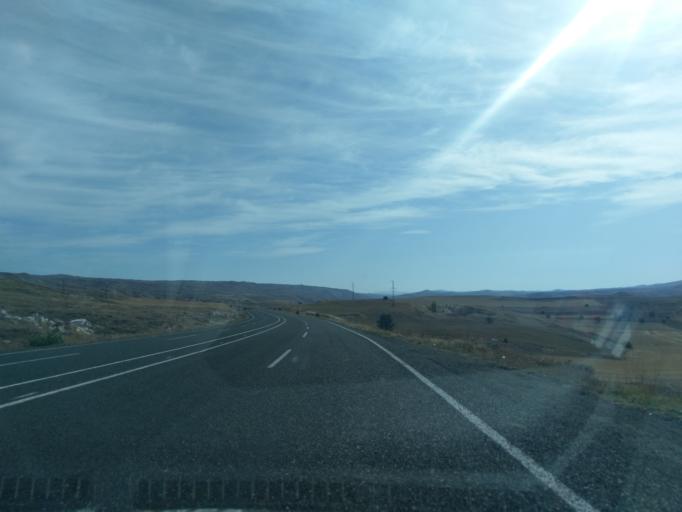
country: TR
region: Sivas
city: Zara
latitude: 39.8606
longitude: 37.8860
